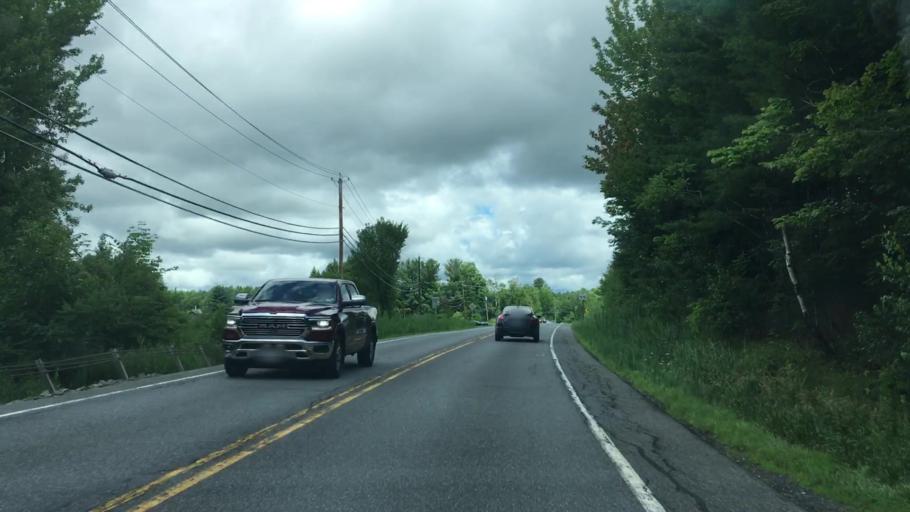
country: US
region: New York
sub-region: Rensselaer County
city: Hoosick Falls
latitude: 42.8406
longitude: -73.4815
